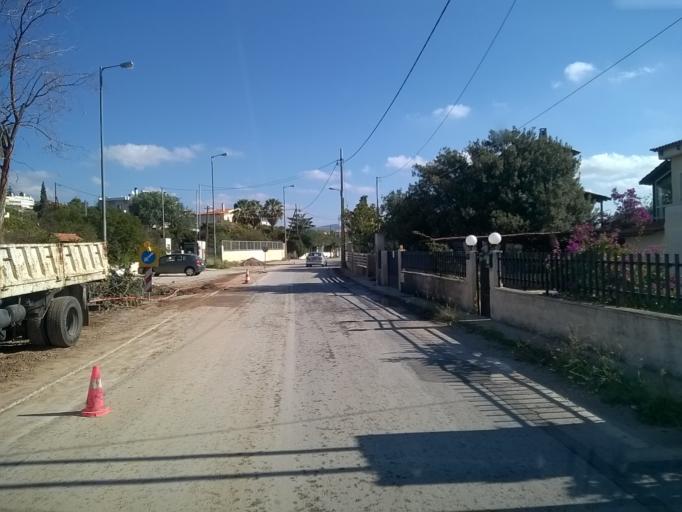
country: GR
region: Attica
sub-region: Nomarchia Anatolikis Attikis
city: Anavyssos
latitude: 37.7360
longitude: 23.9332
